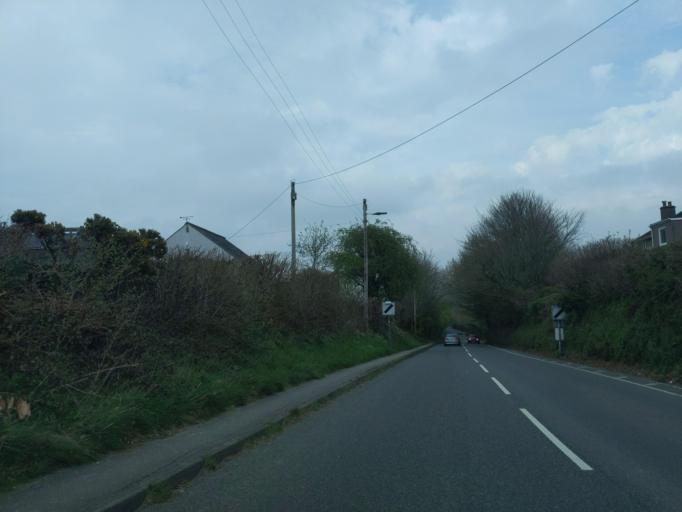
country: GB
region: England
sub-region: Devon
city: Yelverton
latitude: 50.4945
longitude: -4.0808
